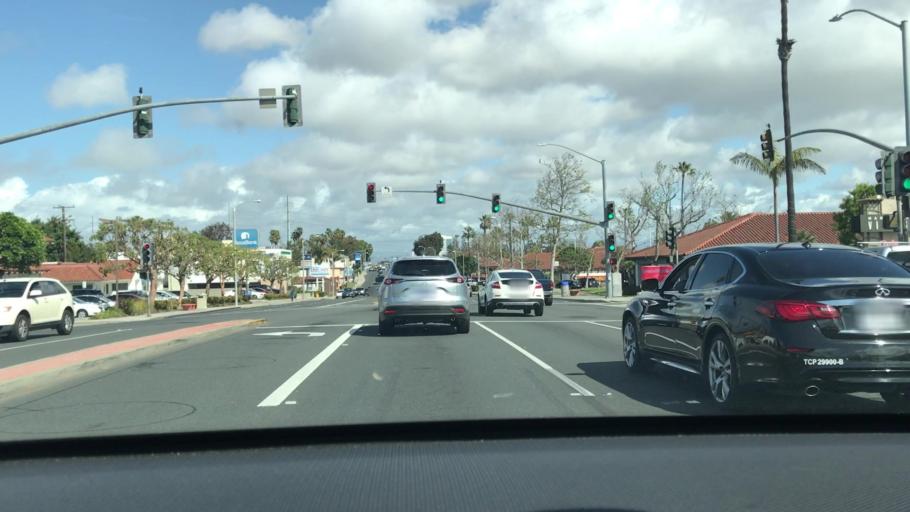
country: US
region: California
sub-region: Los Angeles County
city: Manhattan Beach
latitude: 33.8969
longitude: -118.3960
